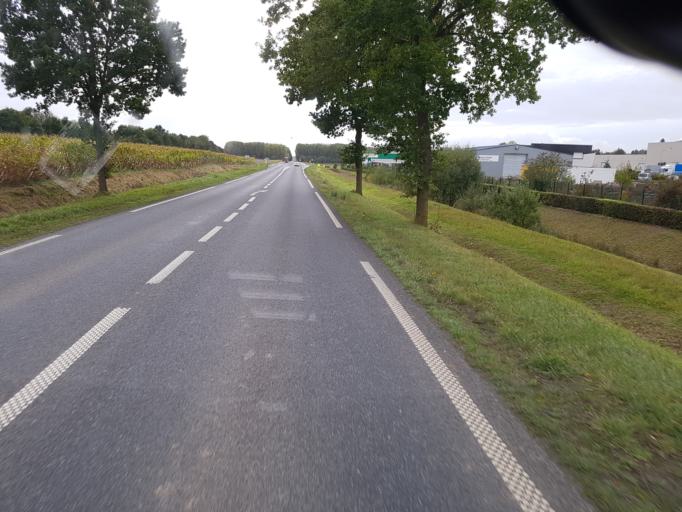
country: FR
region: Nord-Pas-de-Calais
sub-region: Departement du Pas-de-Calais
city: Avesnes-le-Comte
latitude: 50.2055
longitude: 2.5387
